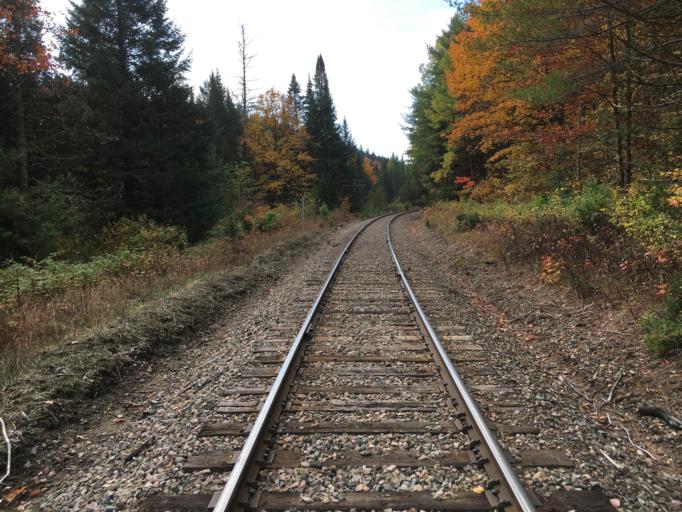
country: US
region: Vermont
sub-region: Caledonia County
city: Lyndonville
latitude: 44.5932
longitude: -71.9745
